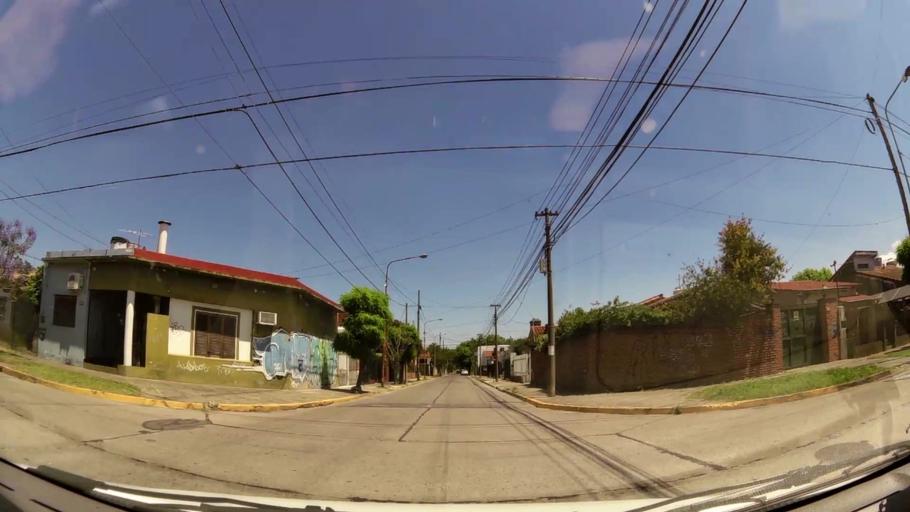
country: AR
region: Buenos Aires
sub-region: Partido de Merlo
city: Merlo
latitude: -34.6650
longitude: -58.7054
